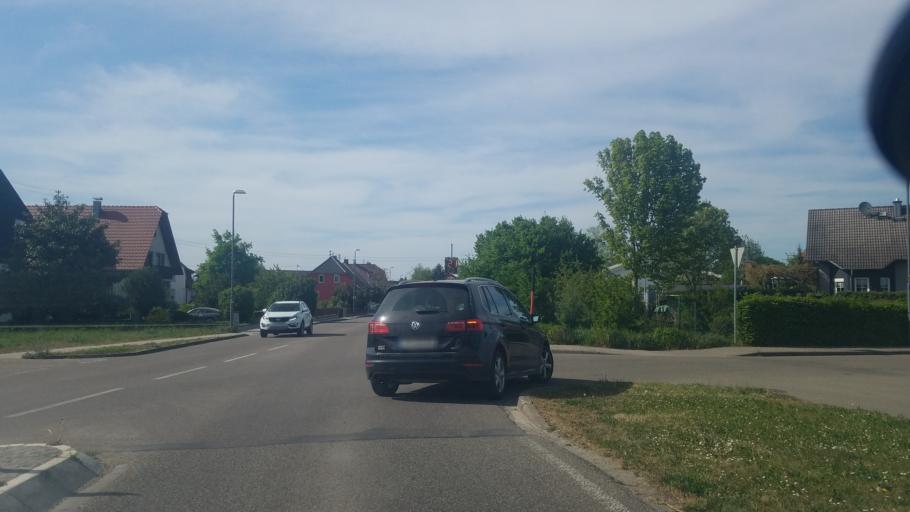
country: DE
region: Baden-Wuerttemberg
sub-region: Freiburg Region
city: Meissenheim
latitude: 48.4606
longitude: 7.8161
